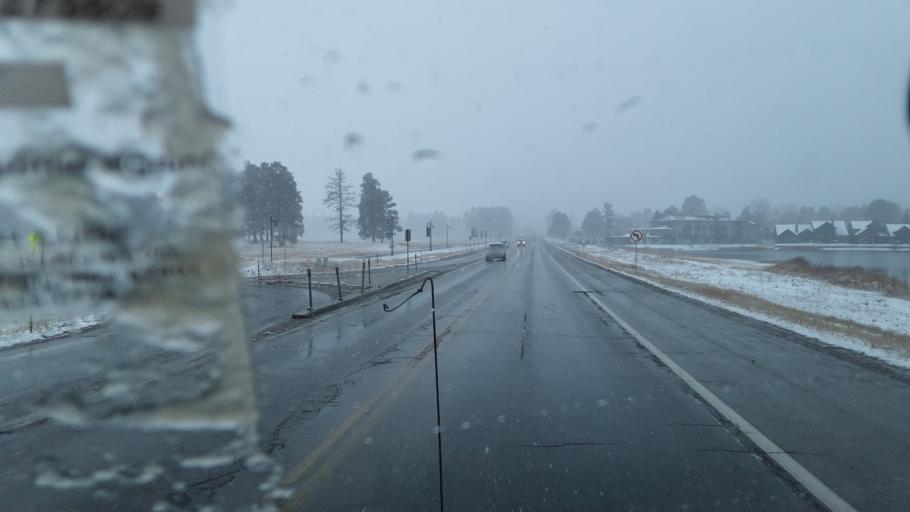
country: US
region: Colorado
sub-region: Archuleta County
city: Pagosa Springs
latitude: 37.2618
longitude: -107.0638
